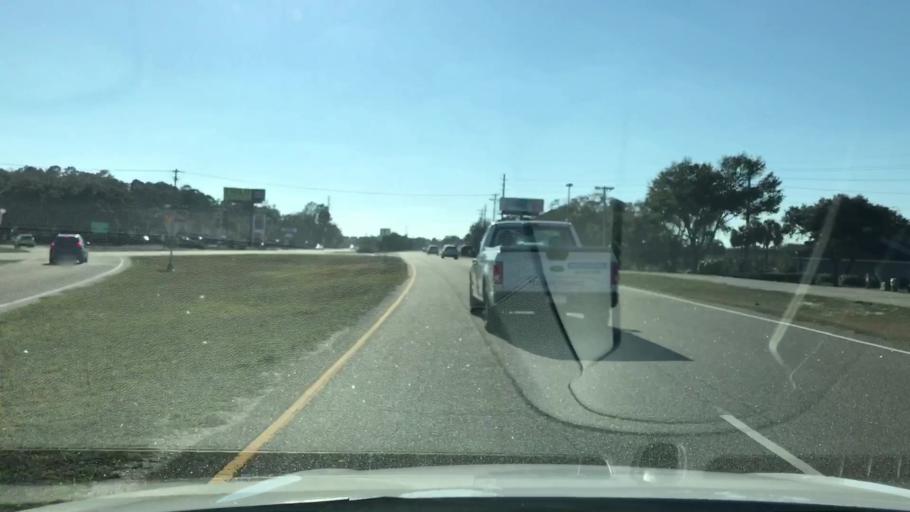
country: US
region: South Carolina
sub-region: Horry County
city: Garden City
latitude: 33.5773
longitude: -79.0249
